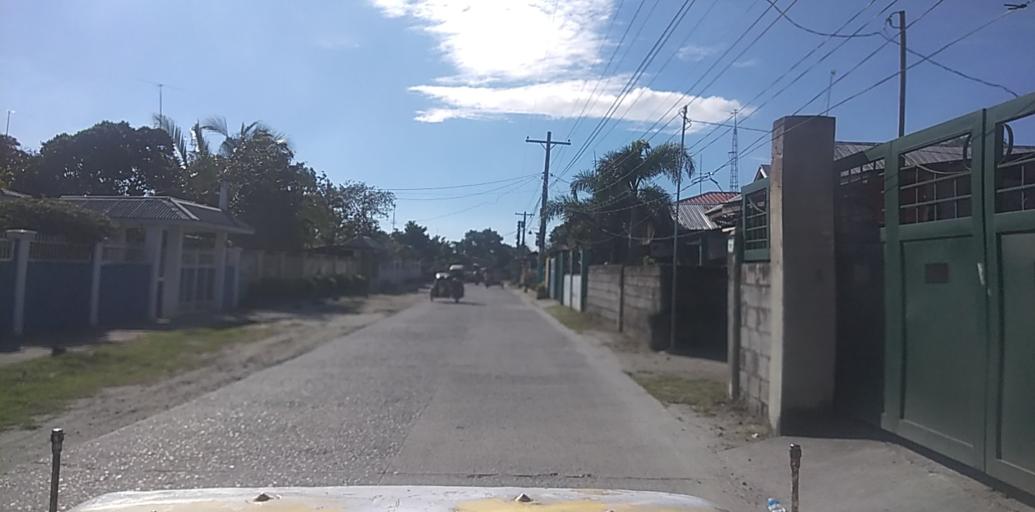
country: PH
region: Central Luzon
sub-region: Province of Pampanga
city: San Patricio
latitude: 15.1080
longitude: 120.7127
